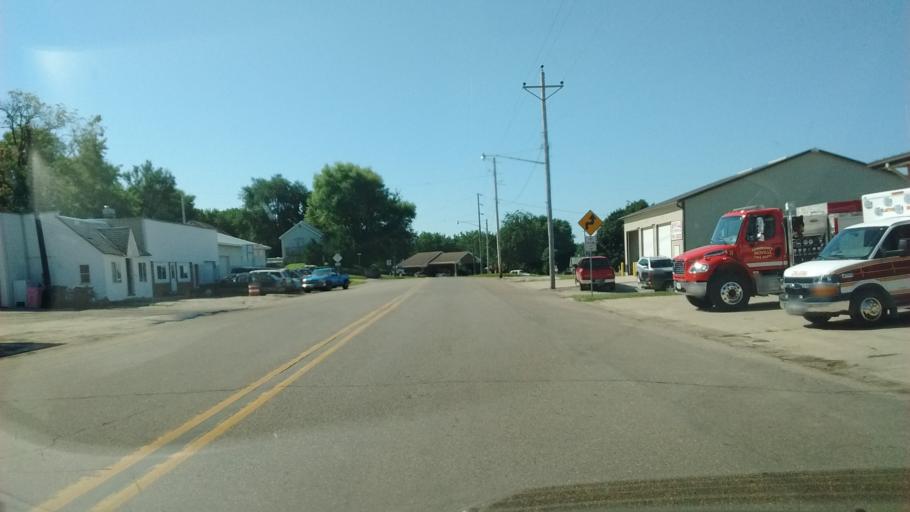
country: US
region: Iowa
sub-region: Woodbury County
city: Moville
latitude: 42.4886
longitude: -96.0751
